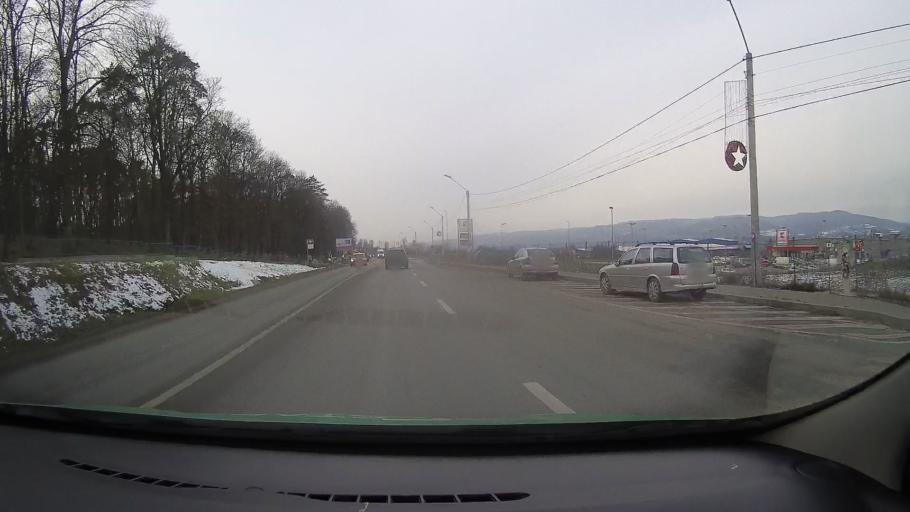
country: RO
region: Hunedoara
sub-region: Municipiul Orastie
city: Orastie
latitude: 45.8379
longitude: 23.1817
